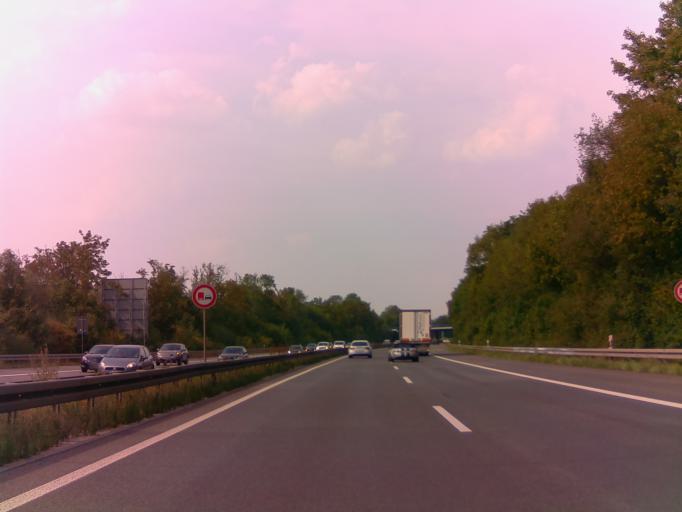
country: DE
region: Hesse
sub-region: Regierungsbezirk Darmstadt
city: Bensheim
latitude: 49.6776
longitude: 8.5994
